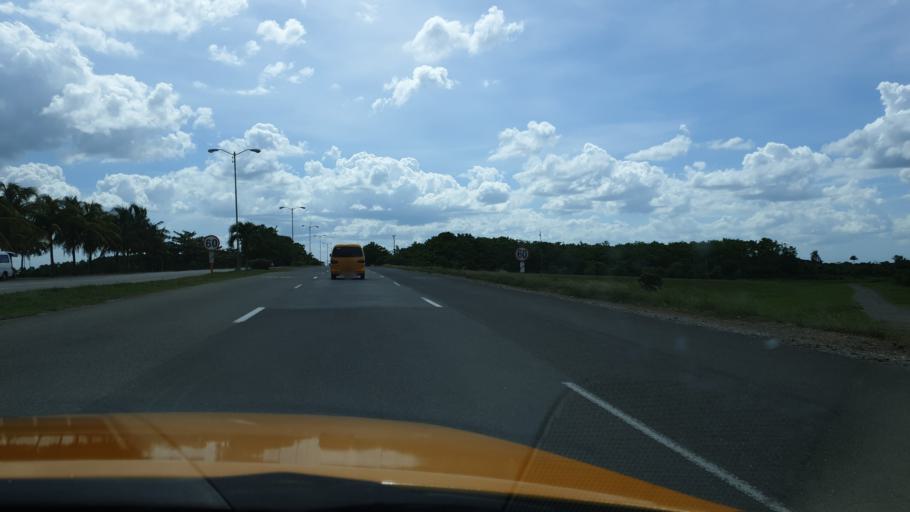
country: CU
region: Cienfuegos
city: Cruces
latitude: 22.4530
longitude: -80.2910
